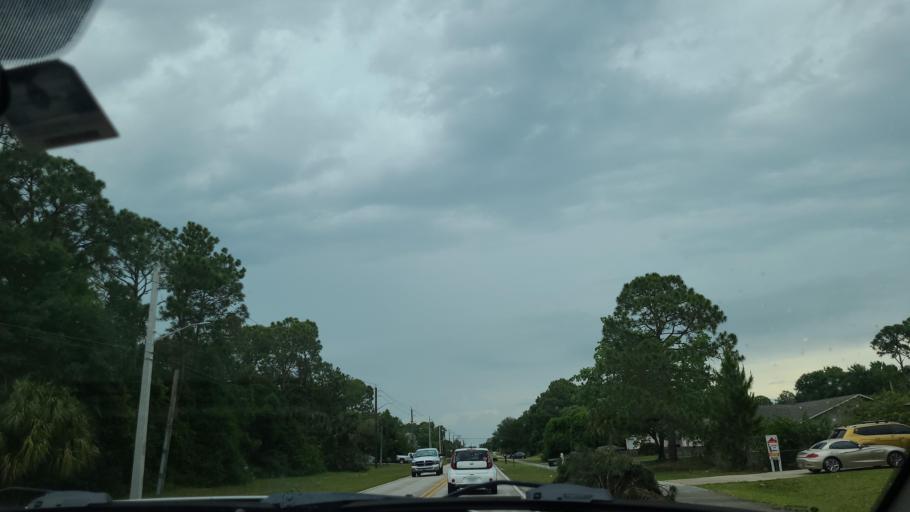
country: US
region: Florida
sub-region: Brevard County
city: June Park
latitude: 28.0086
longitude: -80.6968
